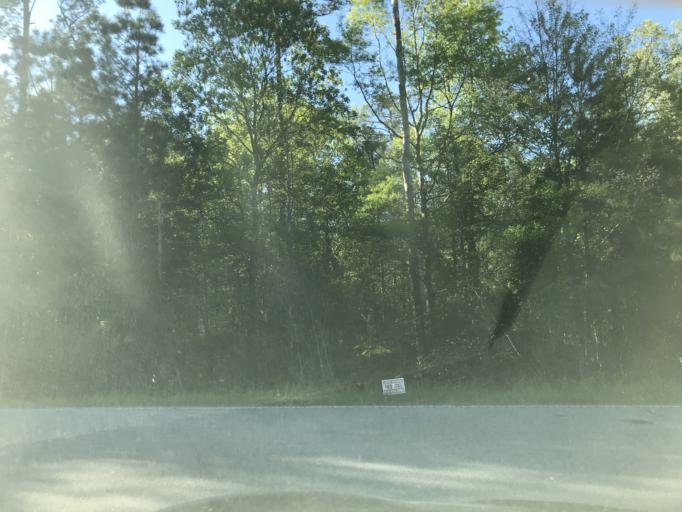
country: US
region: North Carolina
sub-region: Wake County
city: Knightdale
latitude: 35.8130
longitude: -78.5566
